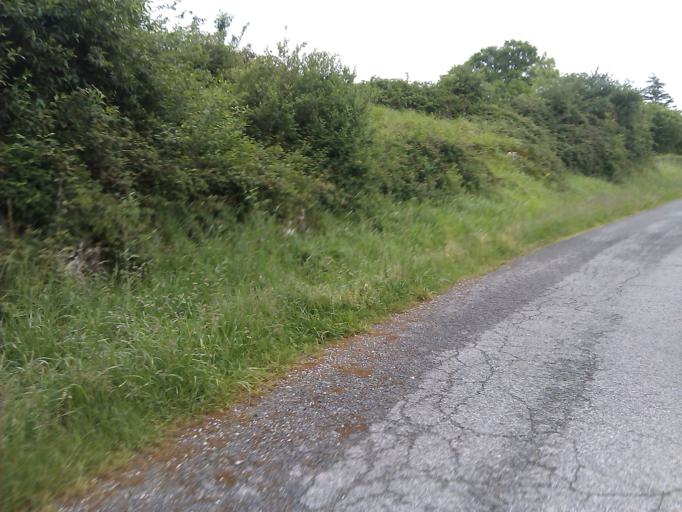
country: ES
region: Navarre
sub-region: Provincia de Navarra
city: Lekunberri
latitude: 42.9946
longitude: -1.8872
